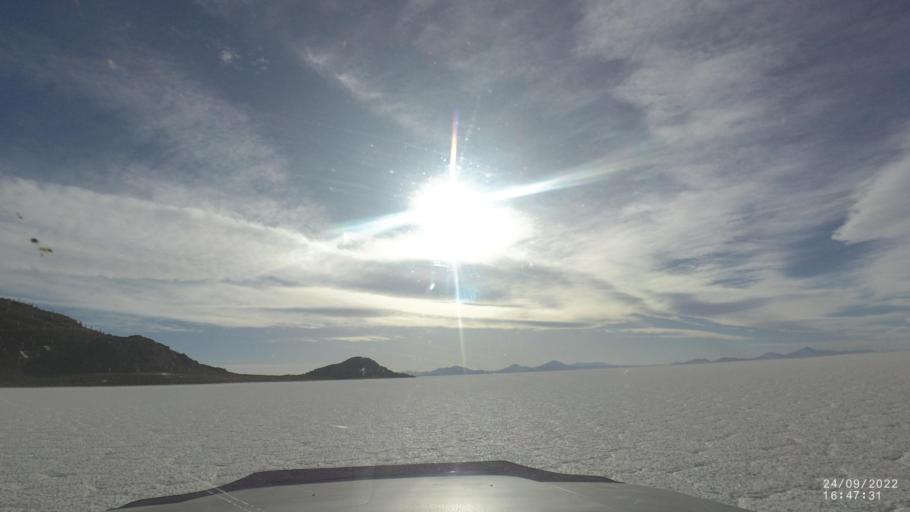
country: BO
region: Potosi
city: Colchani
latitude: -20.1322
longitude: -67.8037
